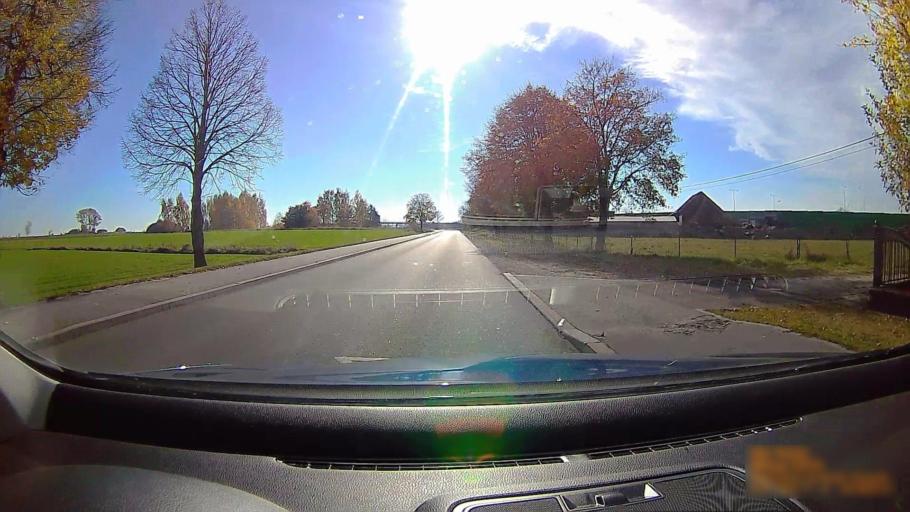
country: PL
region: Greater Poland Voivodeship
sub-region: Powiat kepinski
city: Kepno
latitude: 51.3131
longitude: 18.0143
